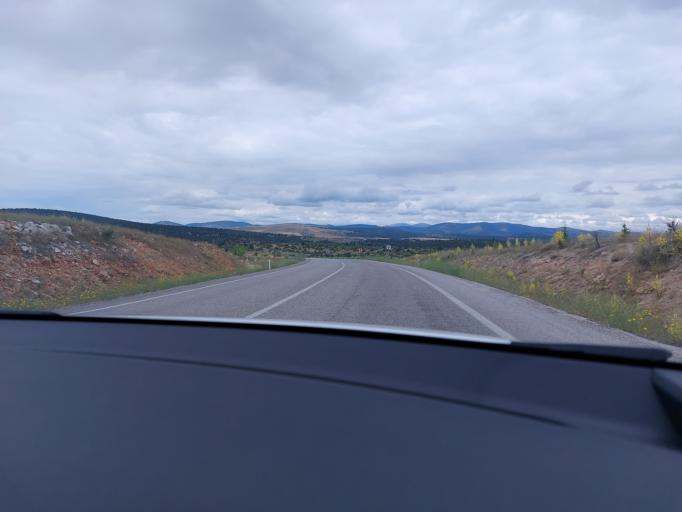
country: TR
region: Konya
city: Doganbey
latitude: 37.8831
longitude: 31.8375
